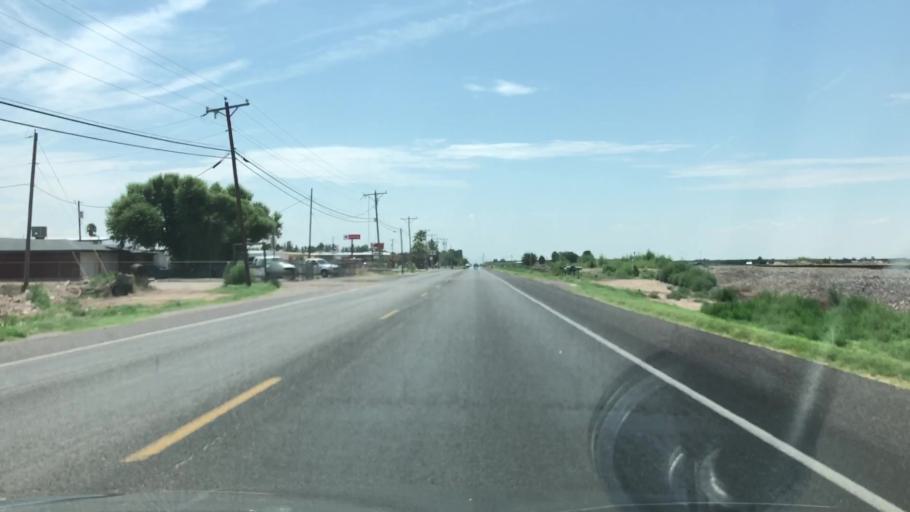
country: US
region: New Mexico
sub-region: Dona Ana County
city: University Park
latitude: 32.2459
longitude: -106.7480
